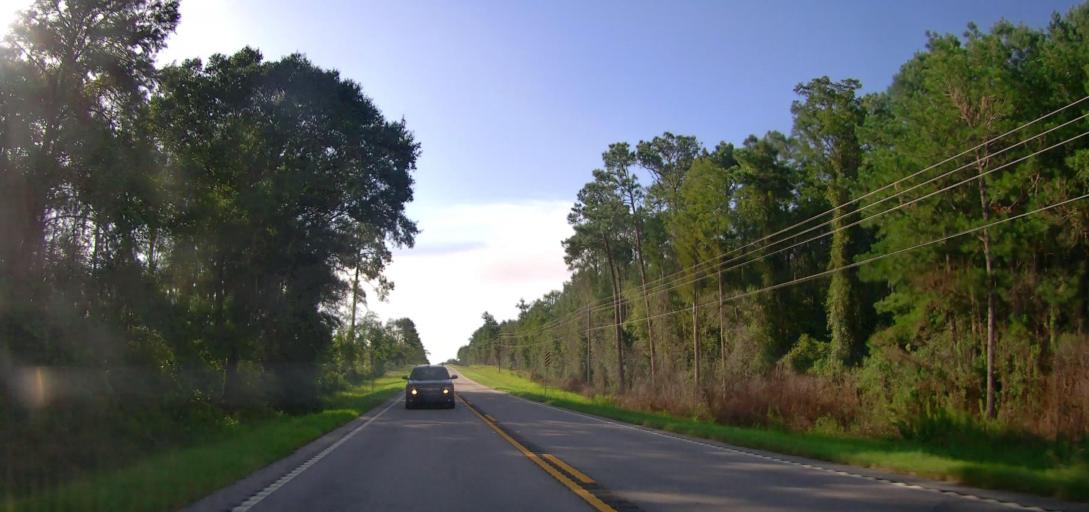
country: US
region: Georgia
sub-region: Coffee County
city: Nicholls
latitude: 31.3996
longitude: -82.6701
